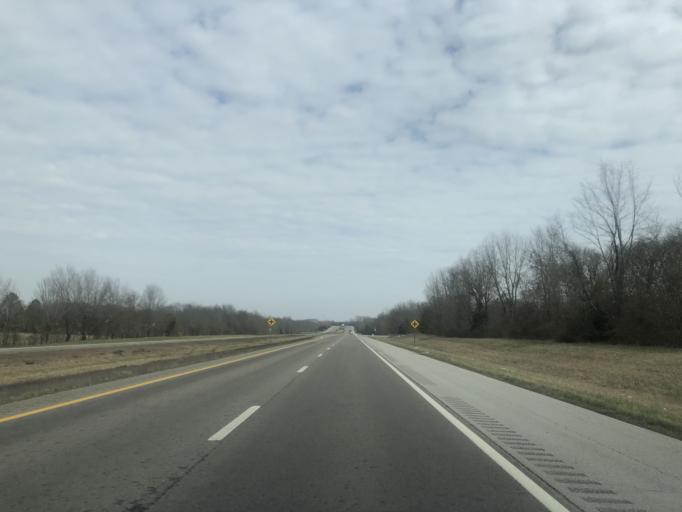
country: US
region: Tennessee
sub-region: Maury County
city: Mount Pleasant
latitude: 35.5846
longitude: -87.1354
